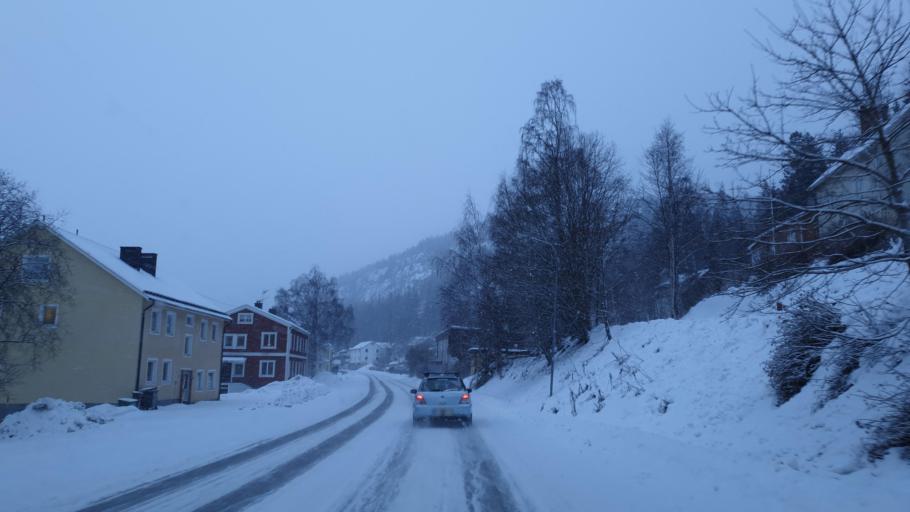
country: SE
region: Vaesternorrland
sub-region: OErnskoeldsviks Kommun
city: Ornskoldsvik
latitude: 63.2973
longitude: 18.6768
